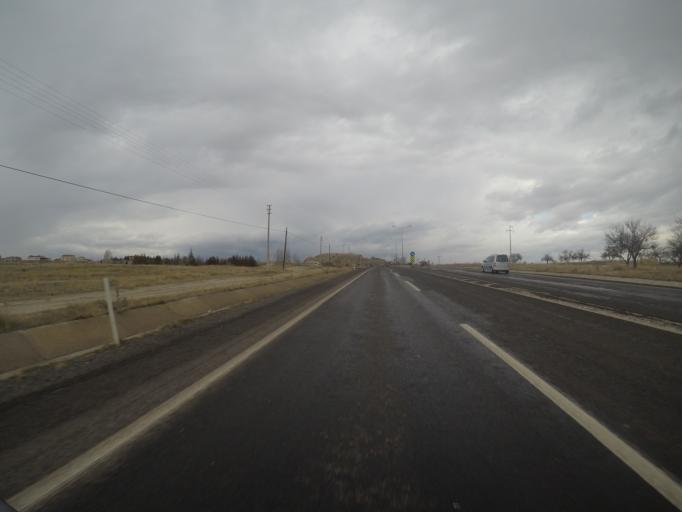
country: TR
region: Nevsehir
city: Goereme
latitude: 38.6345
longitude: 34.8666
